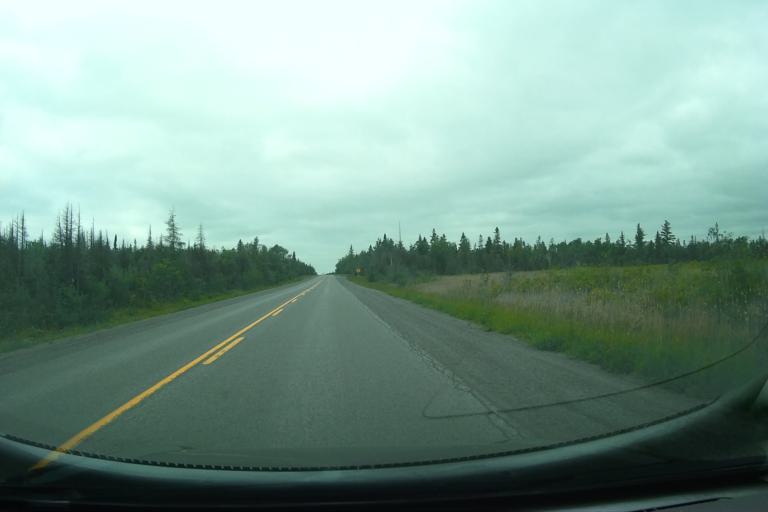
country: CA
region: Ontario
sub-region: Lanark County
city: Smiths Falls
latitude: 45.0065
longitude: -75.8285
